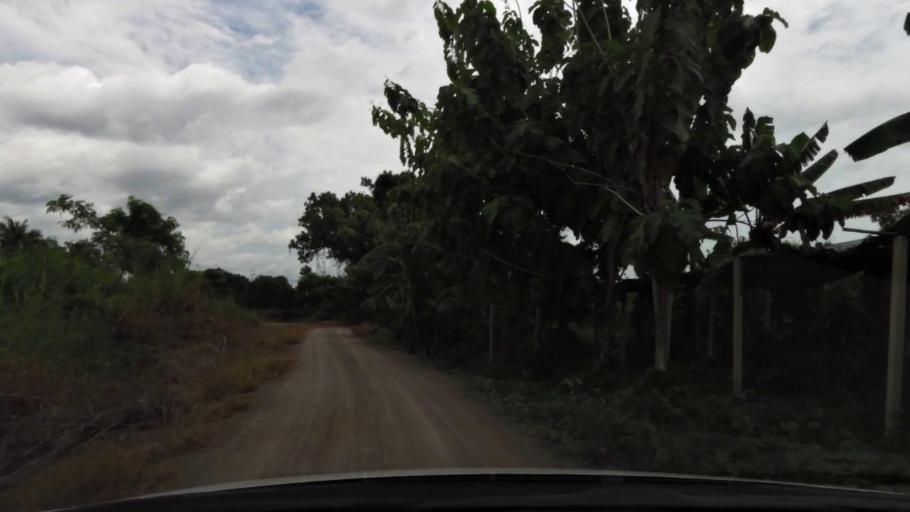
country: TH
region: Samut Sakhon
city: Ban Phaeo
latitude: 13.5577
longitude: 100.0386
